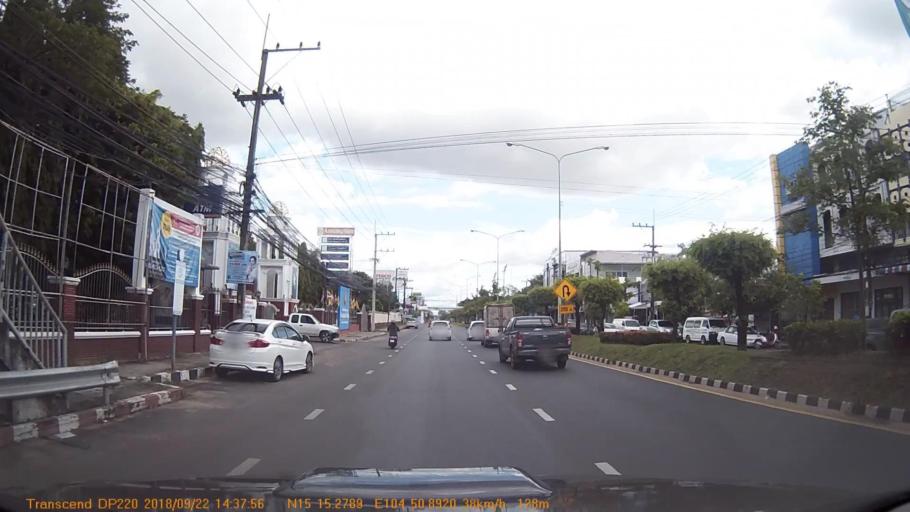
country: TH
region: Changwat Ubon Ratchathani
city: Ubon Ratchathani
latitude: 15.2543
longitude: 104.8483
